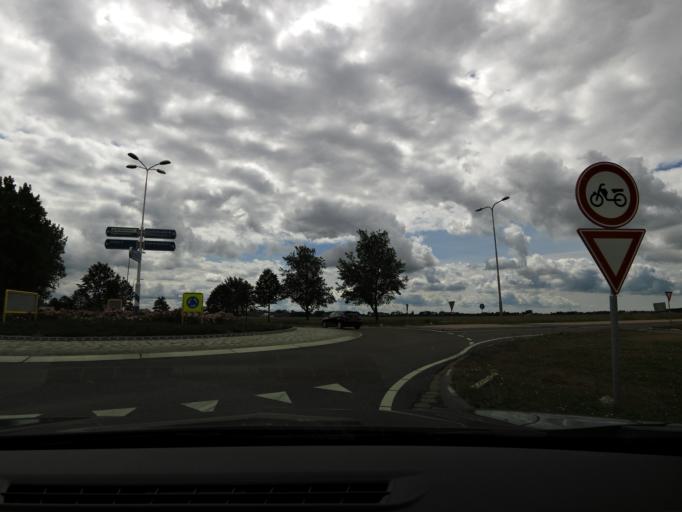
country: NL
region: North Brabant
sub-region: Gemeente Moerdijk
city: Willemstad
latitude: 51.7469
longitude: 4.4416
